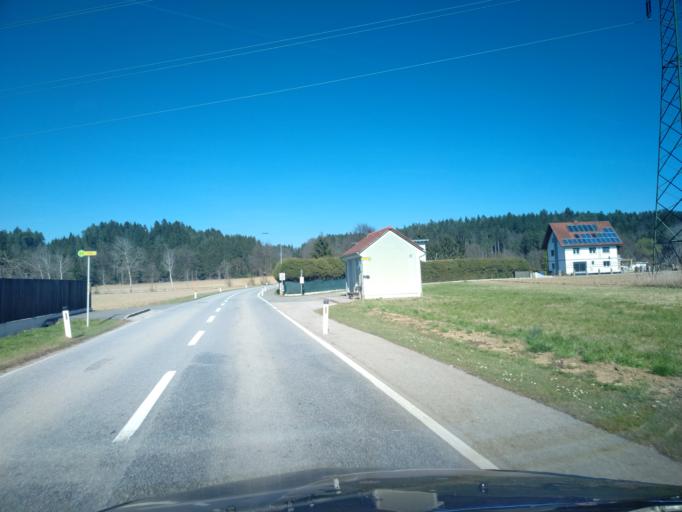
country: AT
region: Styria
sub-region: Politischer Bezirk Graz-Umgebung
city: Zettling
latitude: 46.9124
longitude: 15.4149
